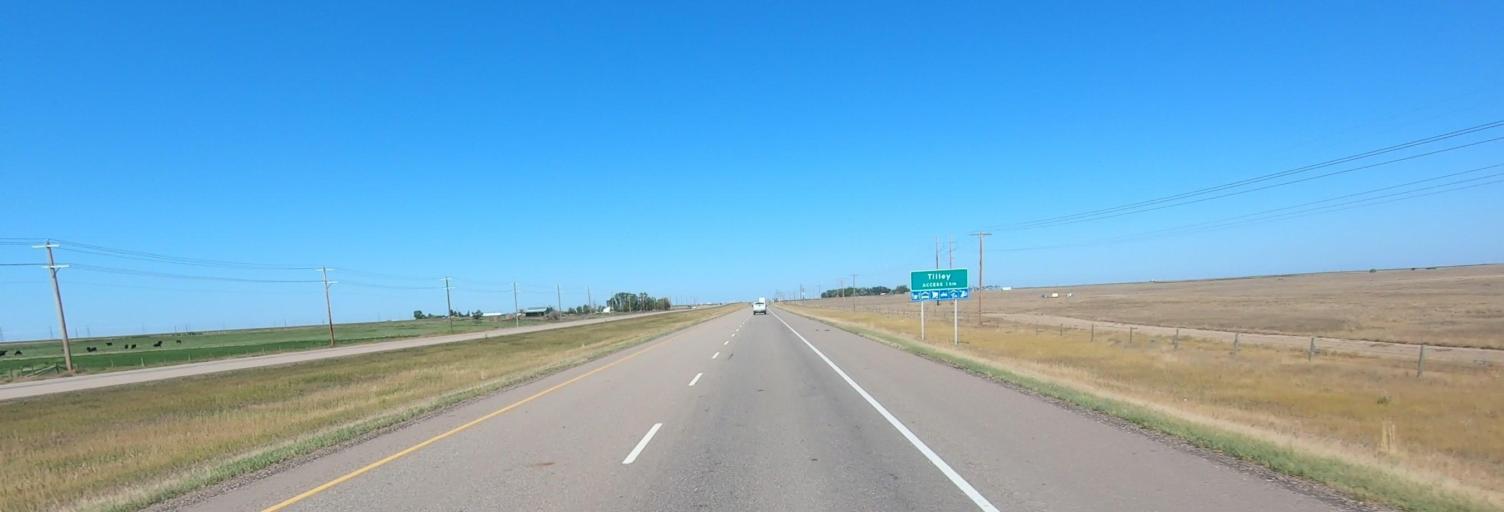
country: CA
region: Alberta
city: Brooks
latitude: 50.4838
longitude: -111.6412
